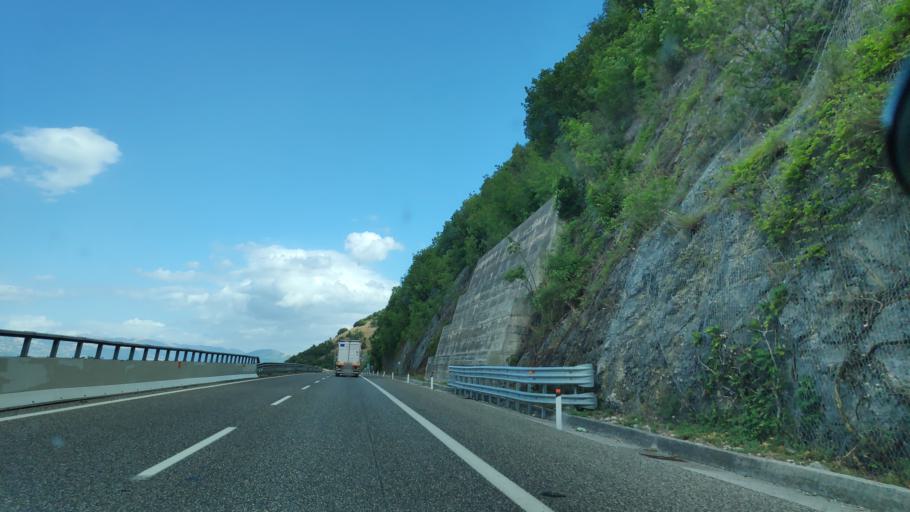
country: IT
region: Campania
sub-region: Provincia di Salerno
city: Sicignano degli Alburni
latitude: 40.5868
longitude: 15.3369
